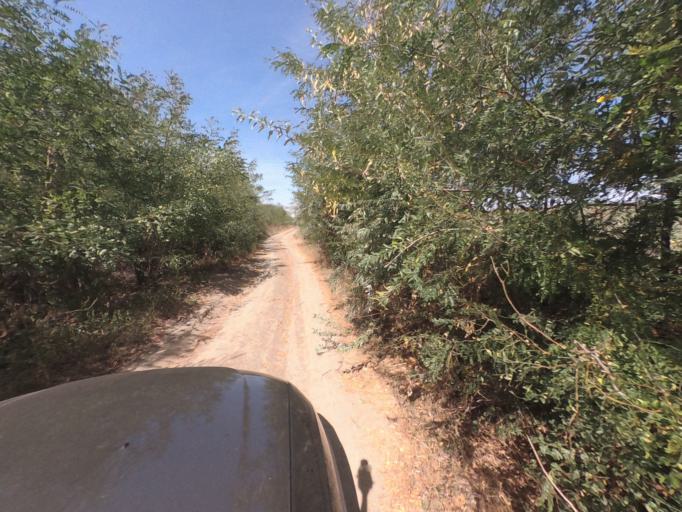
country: RO
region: Vaslui
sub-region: Comuna Costesti
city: Costesti
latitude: 46.5189
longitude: 27.7411
